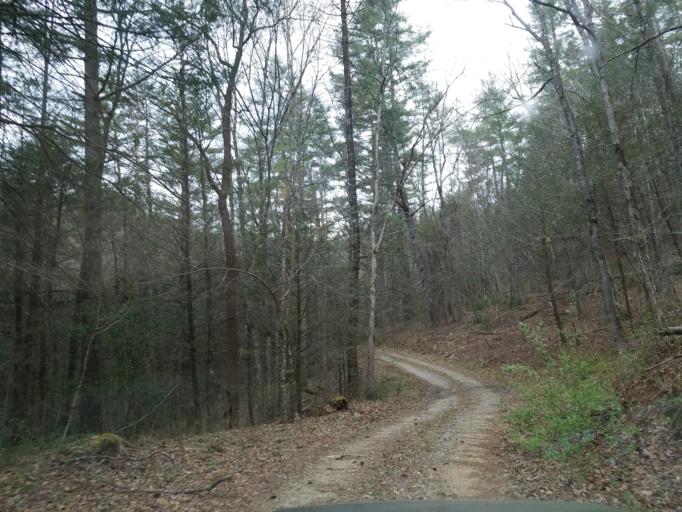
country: US
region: Georgia
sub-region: Union County
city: Blairsville
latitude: 34.7779
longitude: -84.1005
